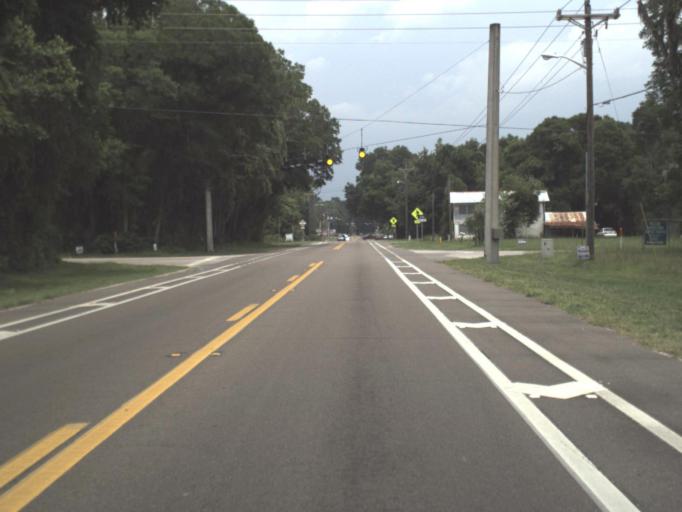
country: US
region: Florida
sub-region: Levy County
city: Chiefland
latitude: 29.4965
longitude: -82.8733
